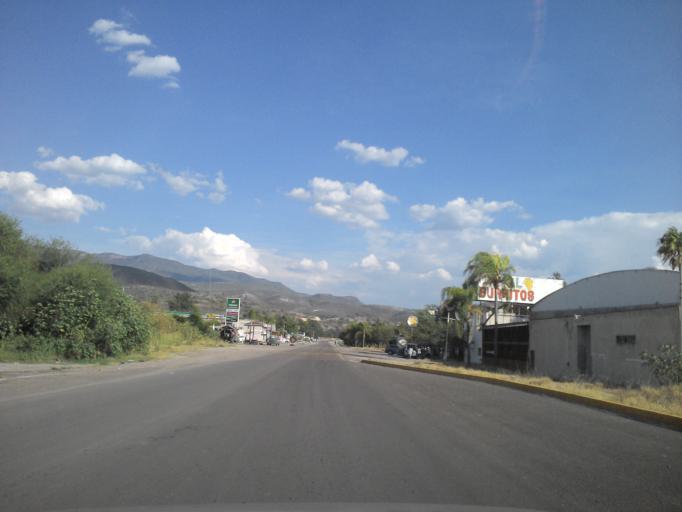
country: MX
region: Zacatecas
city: Juchipila
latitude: 21.2637
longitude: -103.1608
